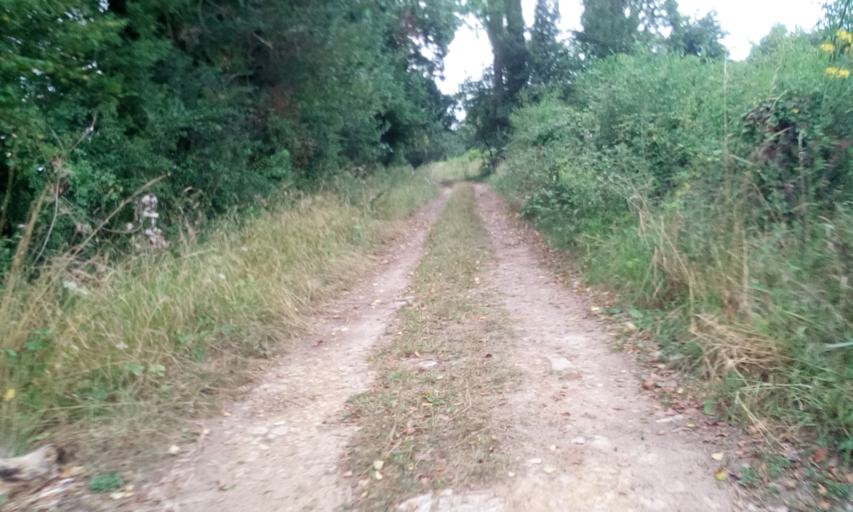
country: FR
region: Lower Normandy
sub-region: Departement du Calvados
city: Sannerville
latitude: 49.1872
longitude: -0.2164
